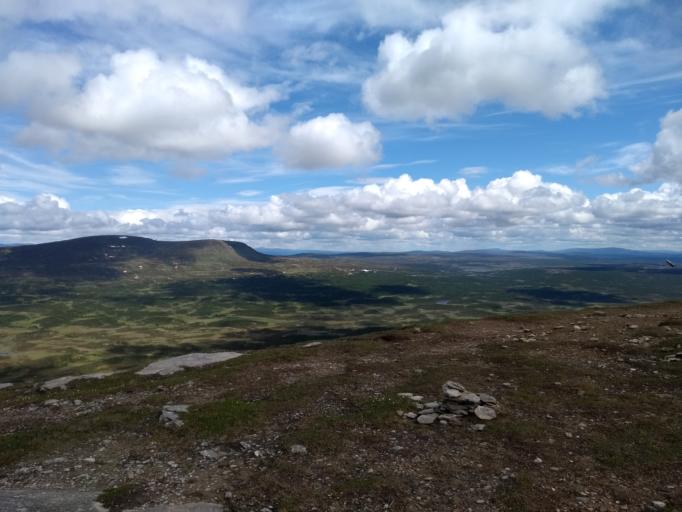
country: NO
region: Sor-Trondelag
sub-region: Tydal
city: Aas
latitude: 62.7332
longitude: 12.4521
